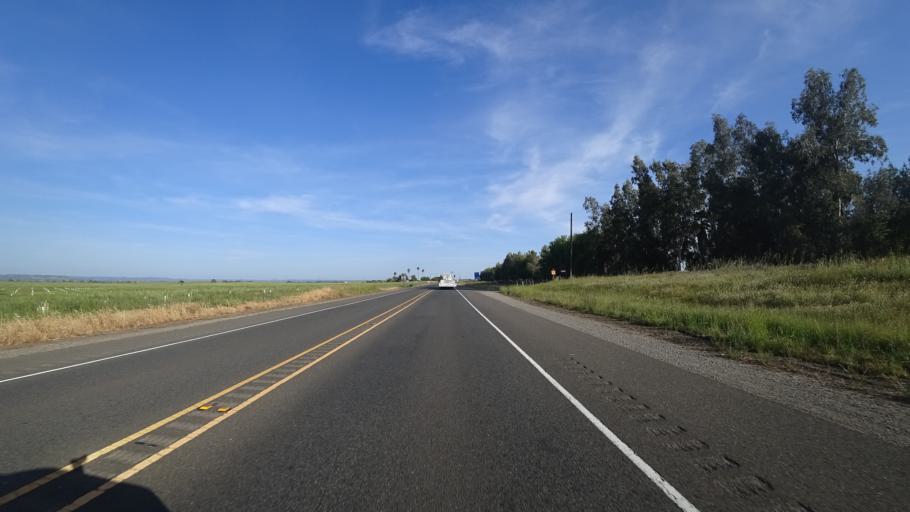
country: US
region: California
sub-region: Placer County
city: Sheridan
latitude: 38.9664
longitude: -121.3643
